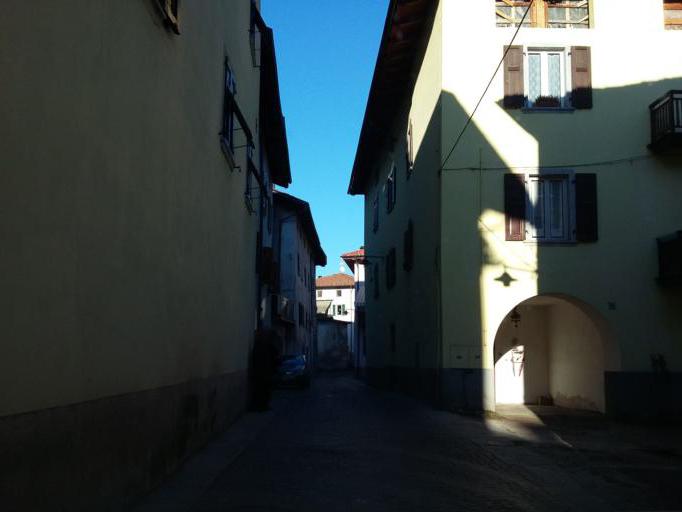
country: IT
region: Trentino-Alto Adige
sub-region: Provincia di Trento
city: Brione
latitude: 45.8926
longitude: 10.6012
